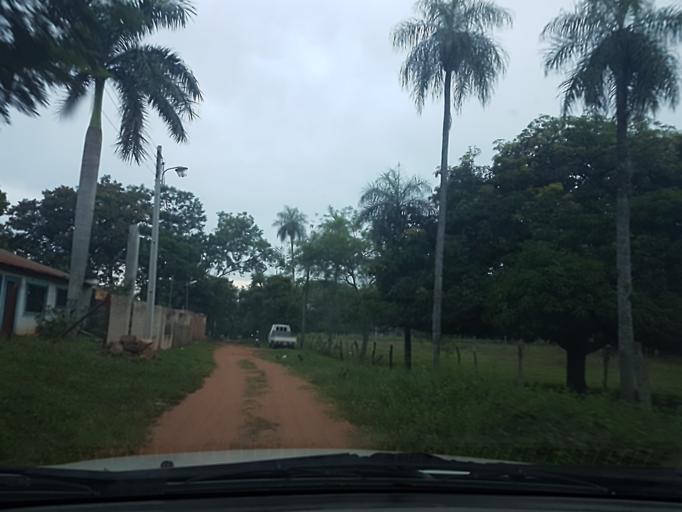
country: PY
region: Central
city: Limpio
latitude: -25.2419
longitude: -57.4609
